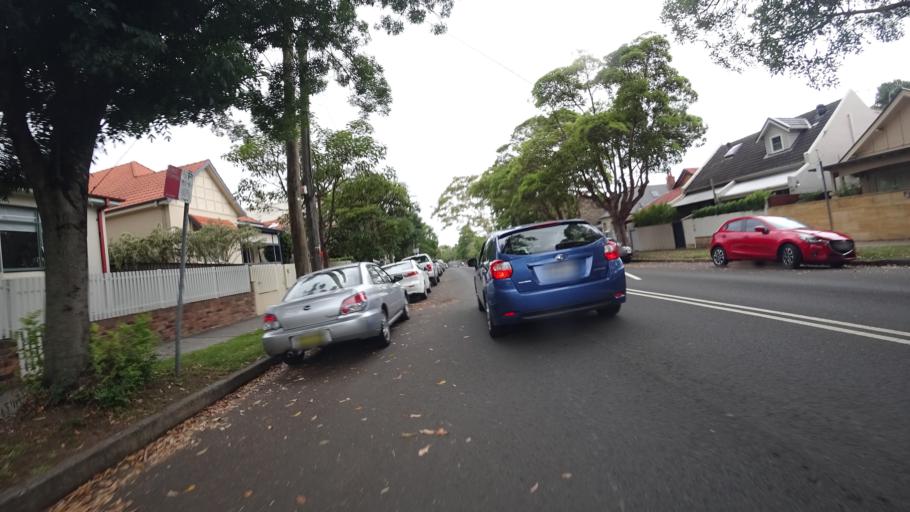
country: AU
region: New South Wales
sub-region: North Sydney
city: Crows Nest
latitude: -33.8303
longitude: 151.2060
